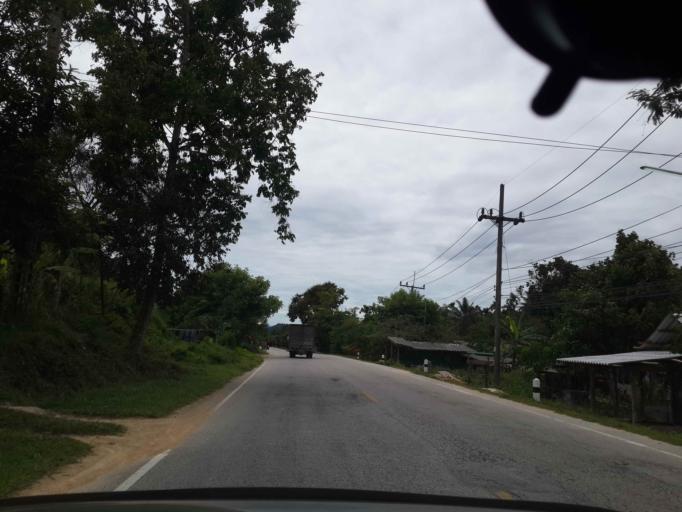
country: TH
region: Narathiwat
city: Rueso
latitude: 6.3579
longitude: 101.6130
